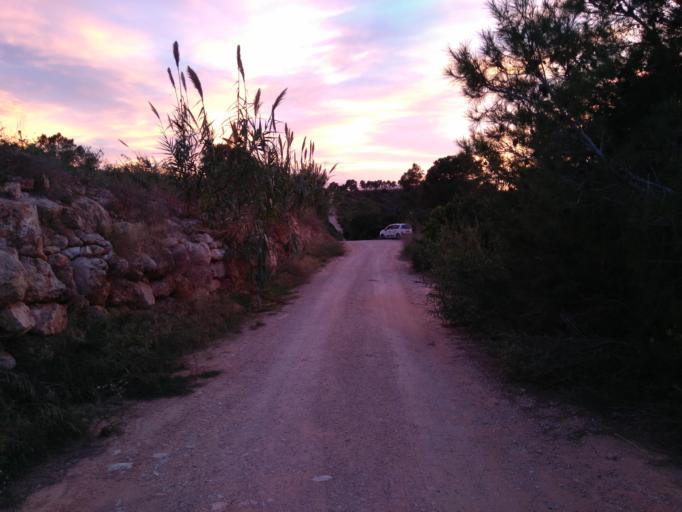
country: ES
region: Valencia
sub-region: Provincia de Valencia
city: Benimodo
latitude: 39.1991
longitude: -0.5733
